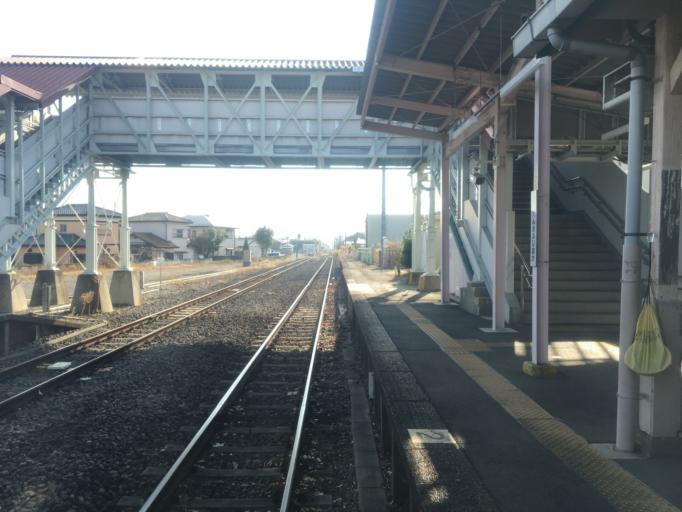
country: JP
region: Gunma
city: Fujioka
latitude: 36.2500
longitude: 139.0834
